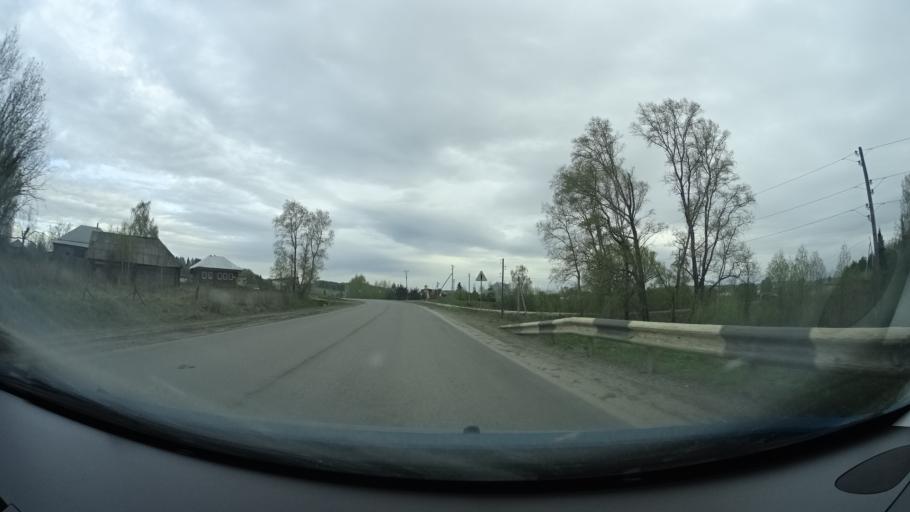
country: RU
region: Perm
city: Osa
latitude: 57.2246
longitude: 55.5874
